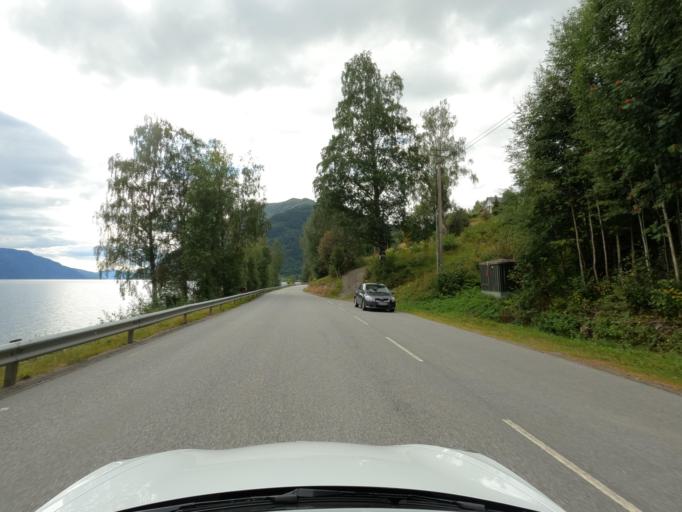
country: NO
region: Telemark
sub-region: Tinn
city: Rjukan
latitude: 59.9540
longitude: 8.8277
